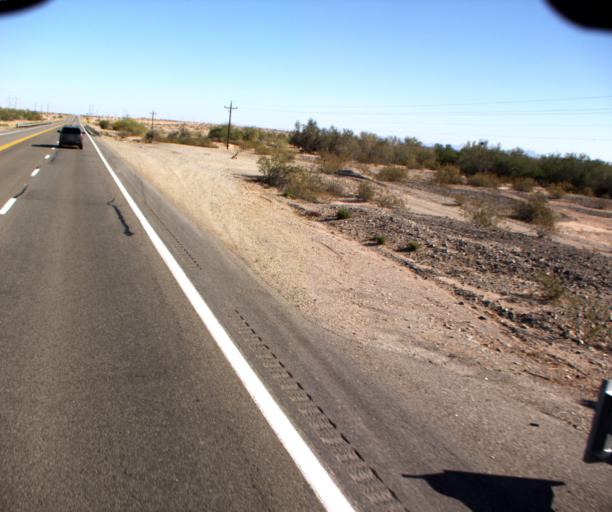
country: US
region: Arizona
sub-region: Yuma County
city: Fortuna Foothills
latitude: 32.7974
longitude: -114.3810
